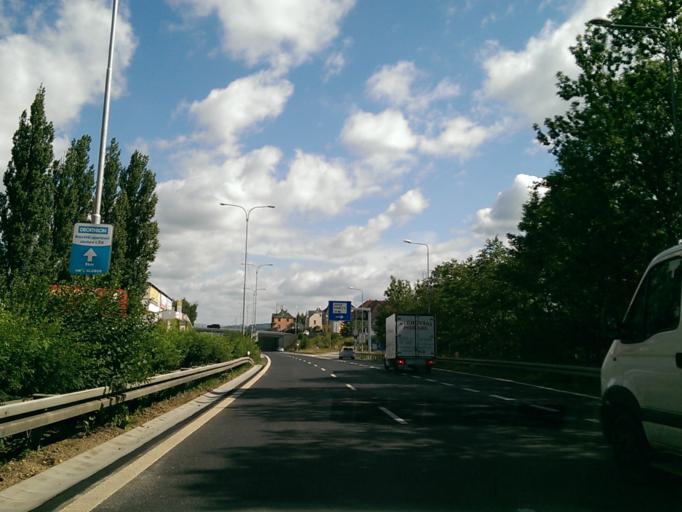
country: CZ
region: Liberecky
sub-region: Okres Liberec
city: Liberec
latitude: 50.7425
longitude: 15.0538
